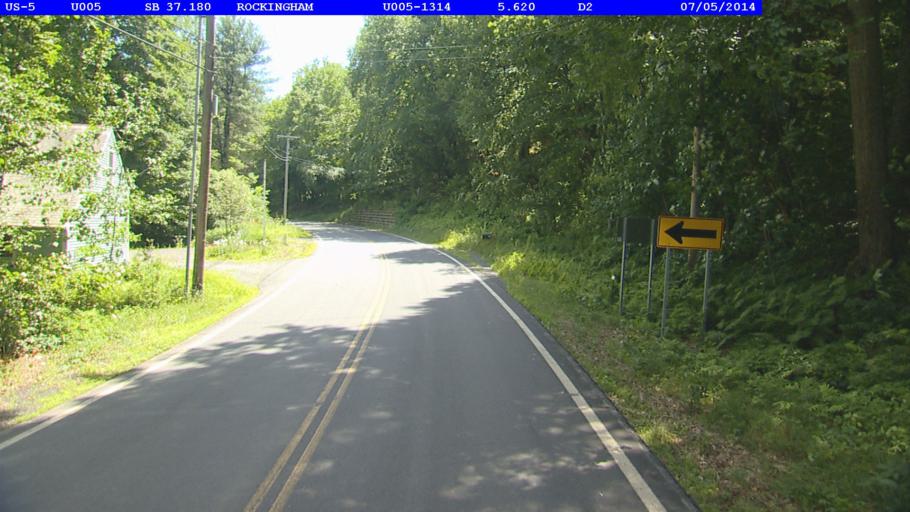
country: US
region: Vermont
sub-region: Windham County
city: Rockingham
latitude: 43.1961
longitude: -72.4533
